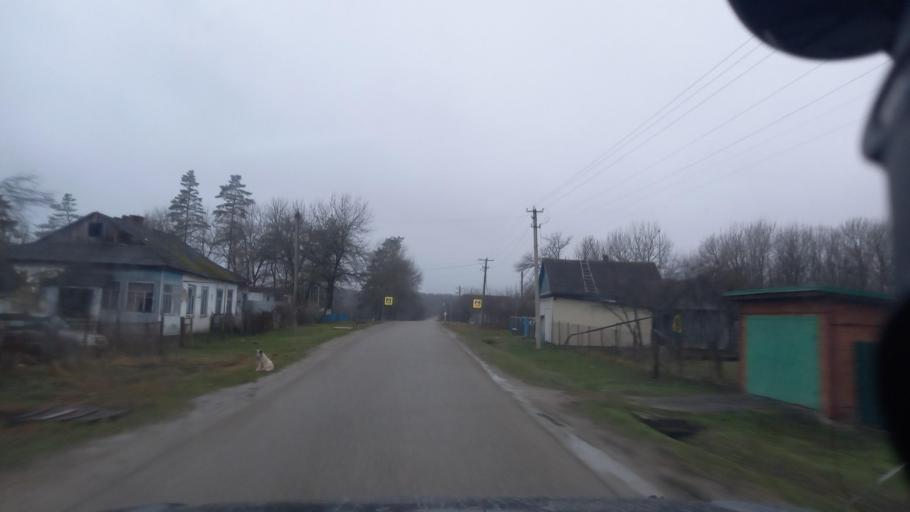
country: RU
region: Krasnodarskiy
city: Saratovskaya
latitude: 44.6477
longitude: 39.3126
